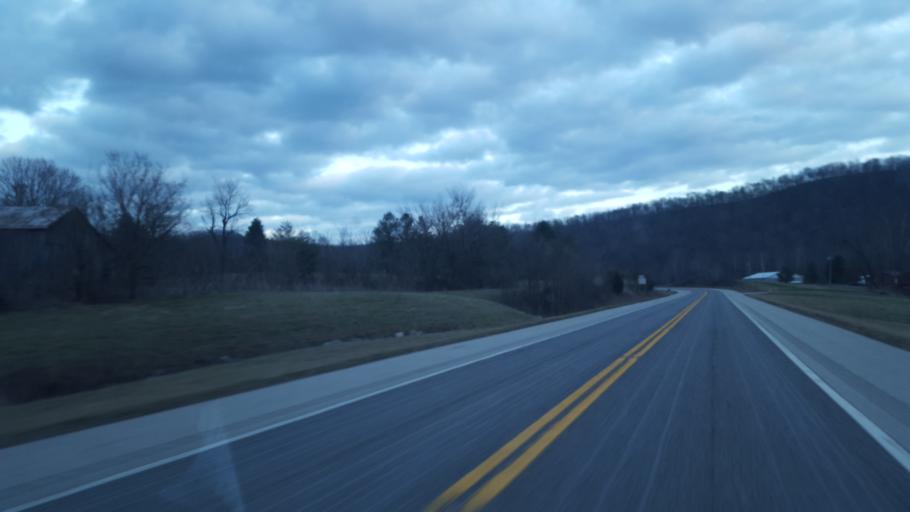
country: US
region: Kentucky
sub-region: Lewis County
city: Vanceburg
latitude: 38.5840
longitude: -83.3670
